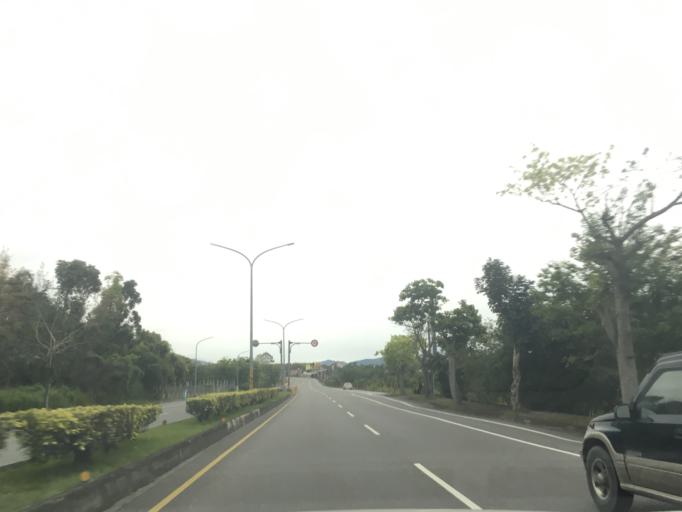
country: TW
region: Taiwan
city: Taitung City
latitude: 22.7229
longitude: 121.0547
